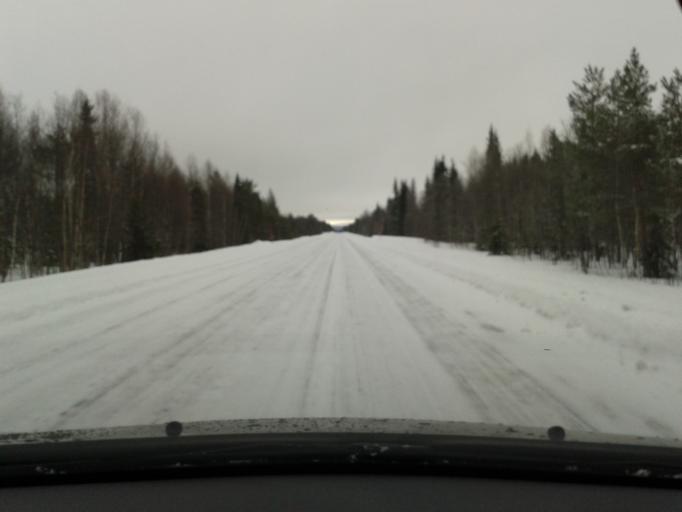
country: SE
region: Vaesterbotten
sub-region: Vilhelmina Kommun
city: Sjoberg
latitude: 64.8504
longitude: 15.9076
